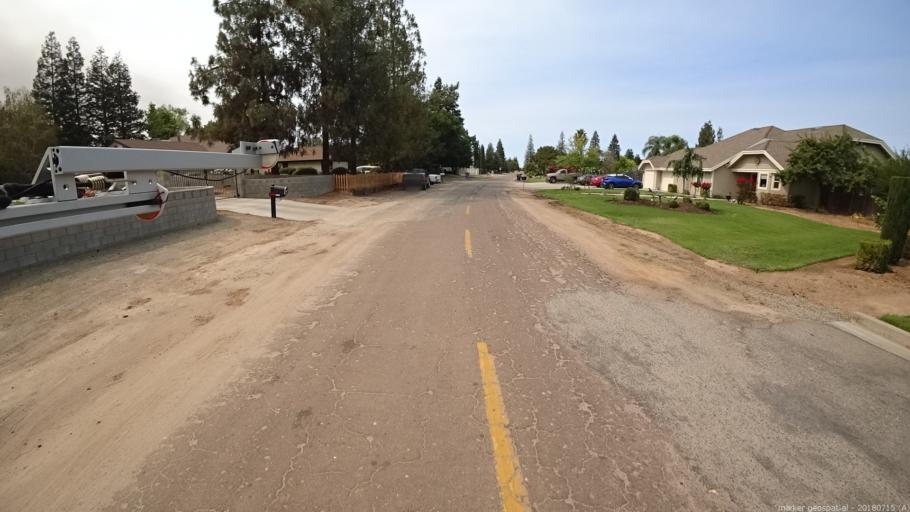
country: US
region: California
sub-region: Madera County
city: Madera Acres
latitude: 37.0236
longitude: -120.0663
